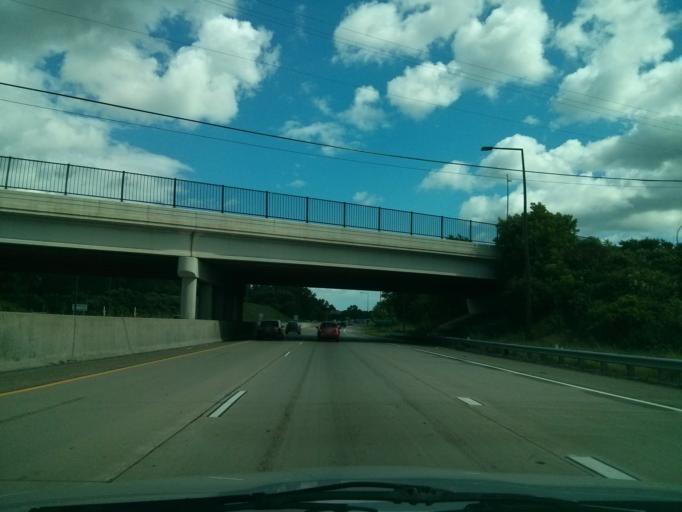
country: US
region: Minnesota
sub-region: Dakota County
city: Mendota Heights
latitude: 44.9017
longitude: -93.1366
